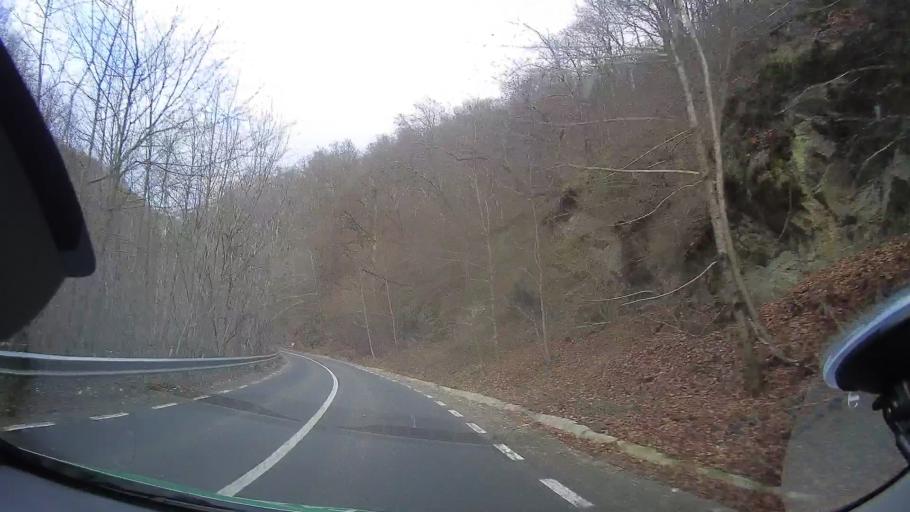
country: RO
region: Cluj
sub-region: Comuna Valea Ierii
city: Valea Ierii
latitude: 46.6316
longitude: 23.3744
